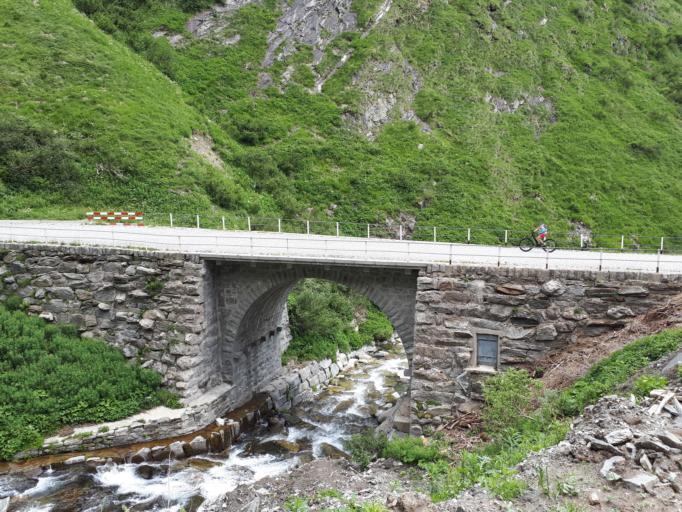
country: CH
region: Ticino
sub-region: Leventina District
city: Airolo
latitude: 46.5411
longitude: 8.5736
